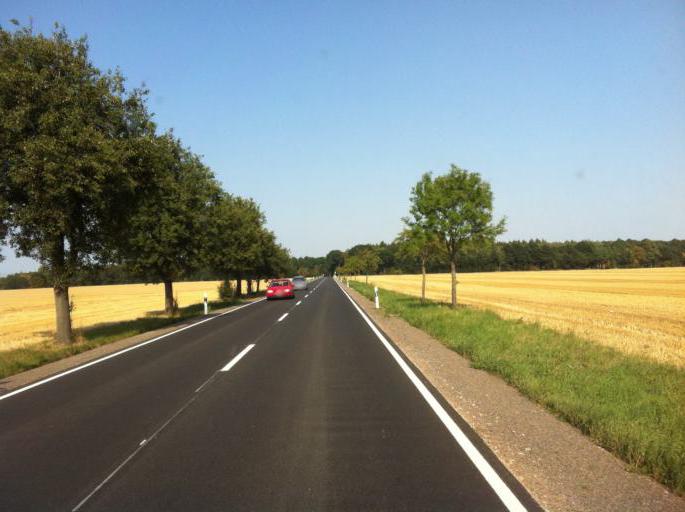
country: DE
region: Thuringia
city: Windischleuba
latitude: 51.0262
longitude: 12.4917
